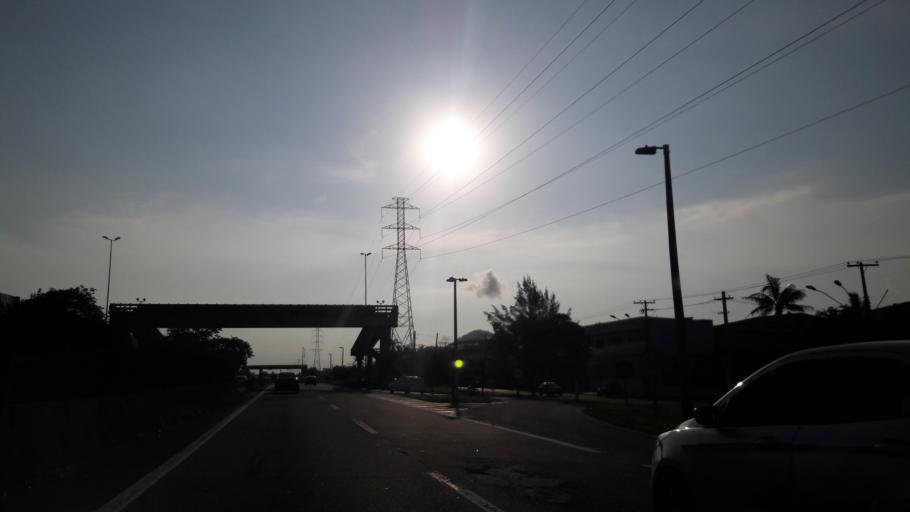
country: BR
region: Sao Paulo
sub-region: Mongagua
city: Mongagua
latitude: -24.1091
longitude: -46.6525
